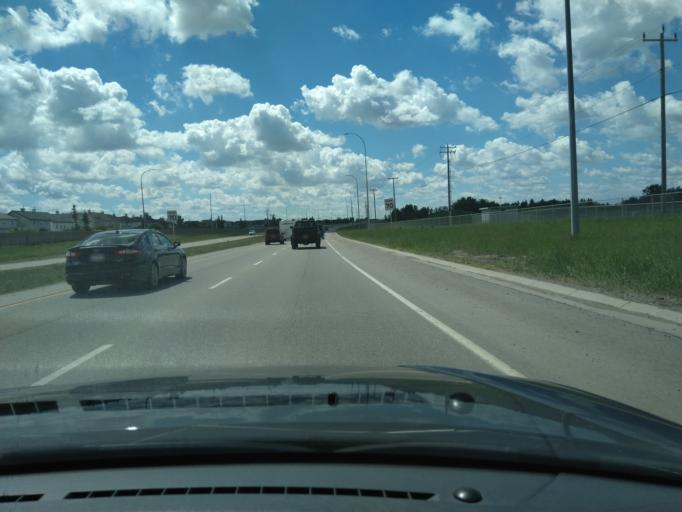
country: CA
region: Alberta
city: Calgary
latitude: 51.1211
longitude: -113.9702
